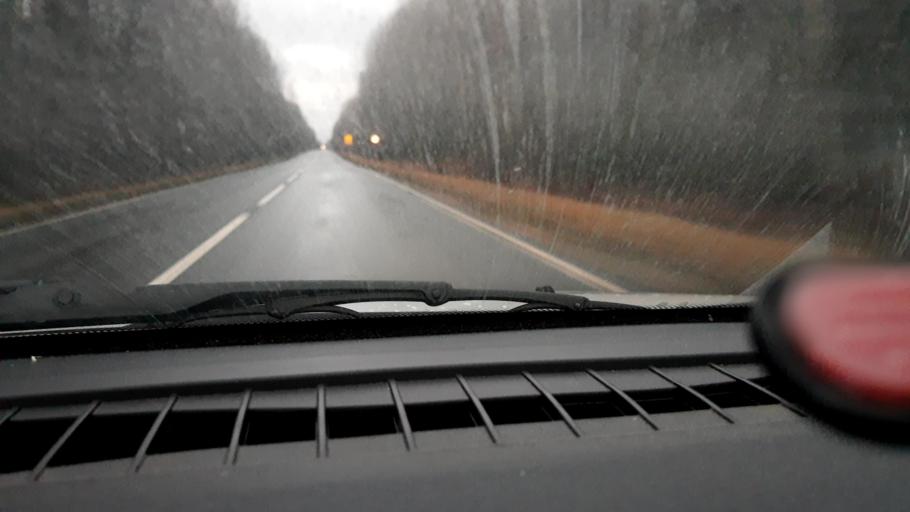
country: RU
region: Nizjnij Novgorod
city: Uren'
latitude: 57.2565
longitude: 45.6105
